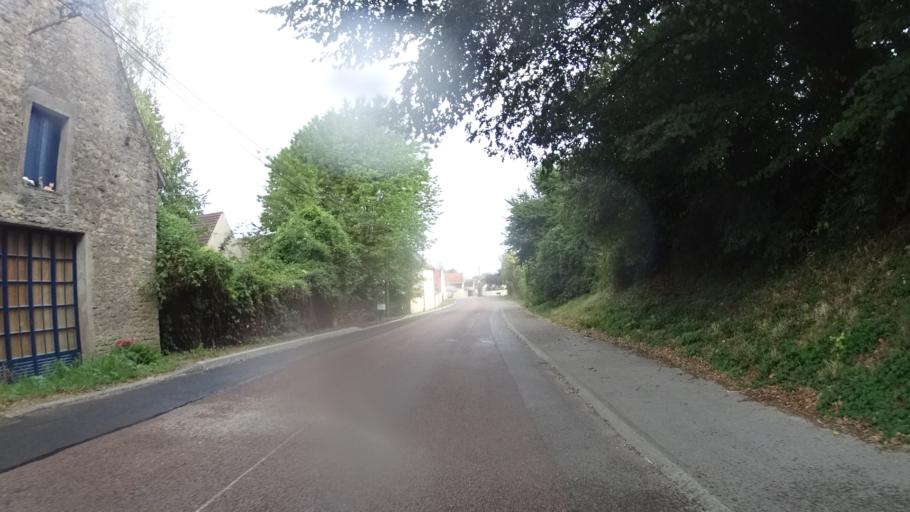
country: FR
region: Bourgogne
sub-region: Departement de Saone-et-Loire
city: Verdun-sur-le-Doubs
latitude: 46.9580
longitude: 5.0283
